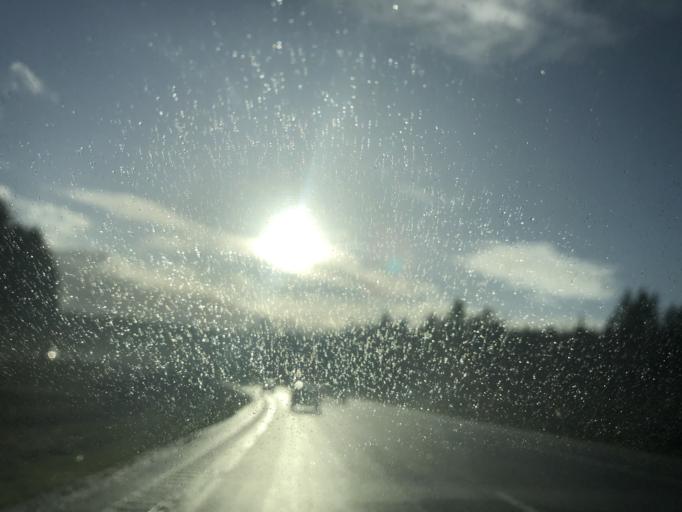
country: US
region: Washington
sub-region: Kitsap County
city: Silverdale
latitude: 47.6588
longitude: -122.7034
